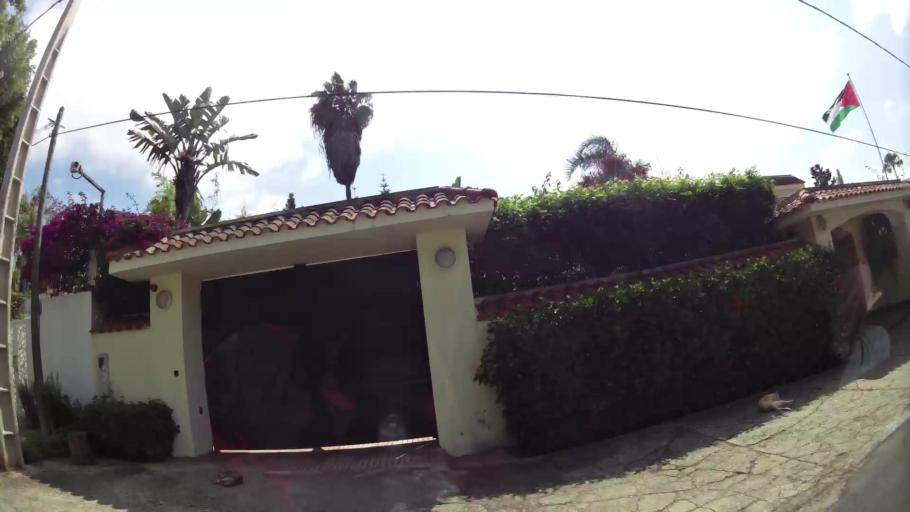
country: MA
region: Rabat-Sale-Zemmour-Zaer
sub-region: Rabat
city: Rabat
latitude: 33.9789
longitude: -6.8392
